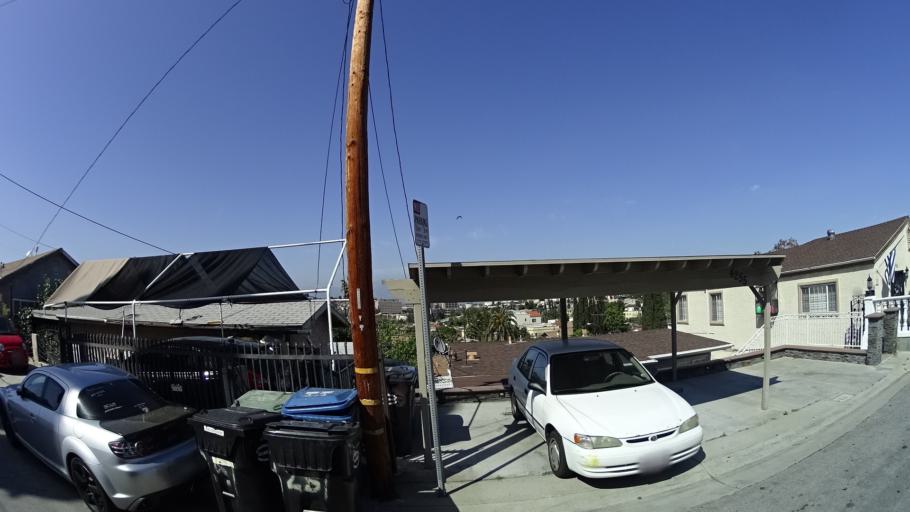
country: US
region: California
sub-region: Los Angeles County
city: Belvedere
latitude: 34.0560
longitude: -118.1737
